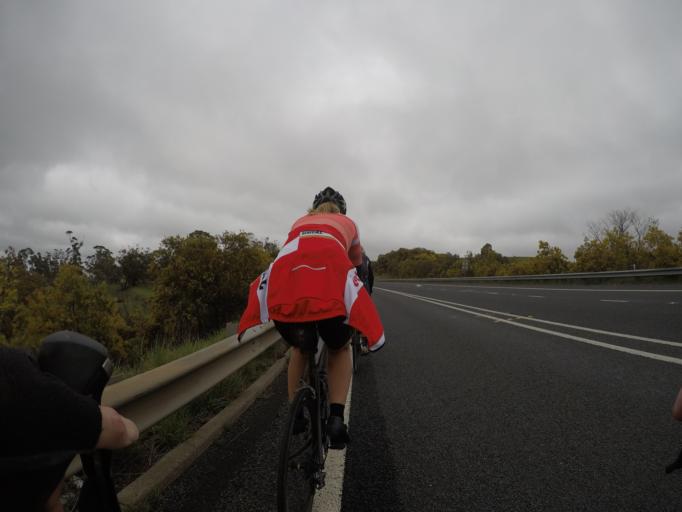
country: AU
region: New South Wales
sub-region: Lithgow
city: Portland
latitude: -33.4514
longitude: 149.9664
